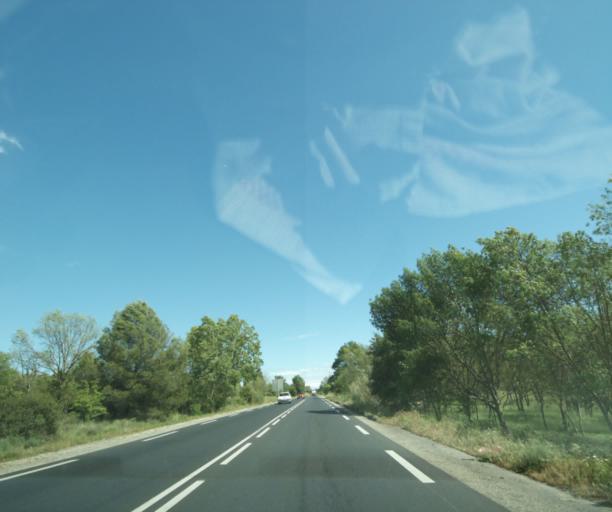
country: FR
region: Languedoc-Roussillon
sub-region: Departement de l'Herault
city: Saint-Jean-de-Vedas
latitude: 43.5889
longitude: 3.8230
